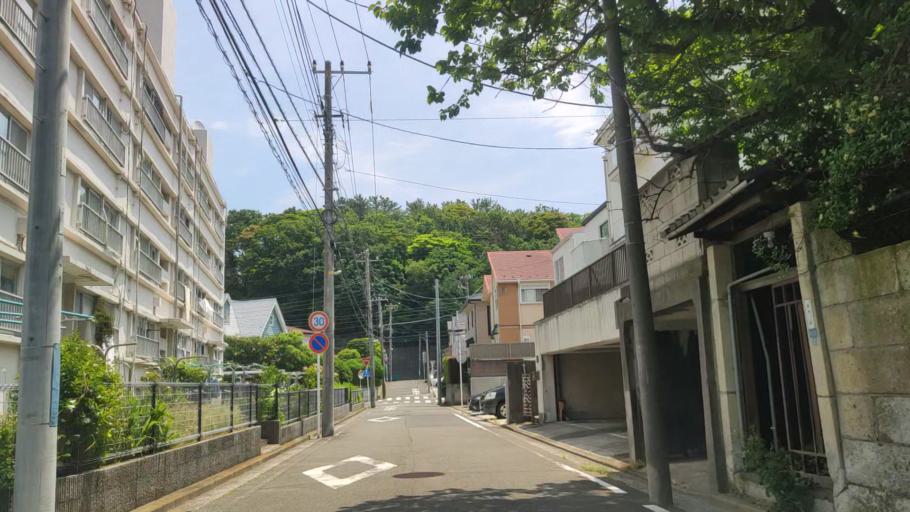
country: JP
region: Kanagawa
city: Yokohama
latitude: 35.4156
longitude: 139.6625
